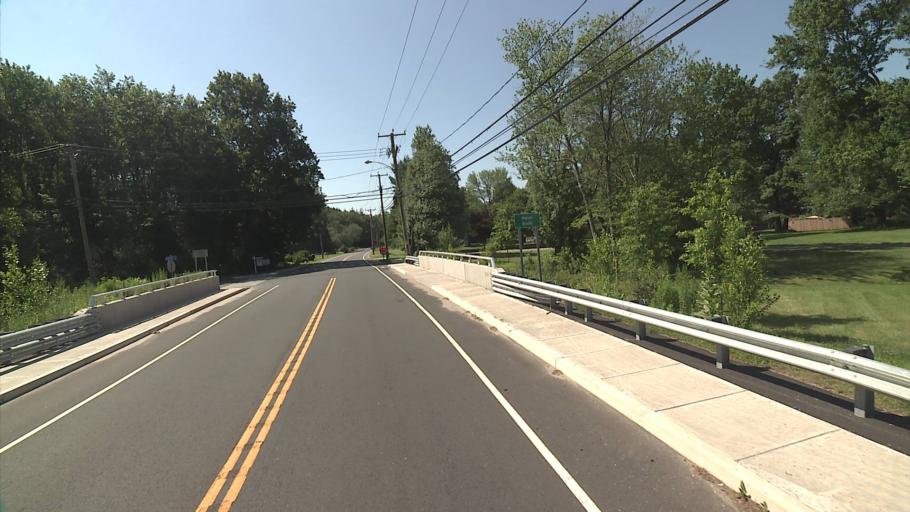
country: US
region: Connecticut
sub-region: Litchfield County
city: Terryville
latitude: 41.6873
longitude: -73.0004
